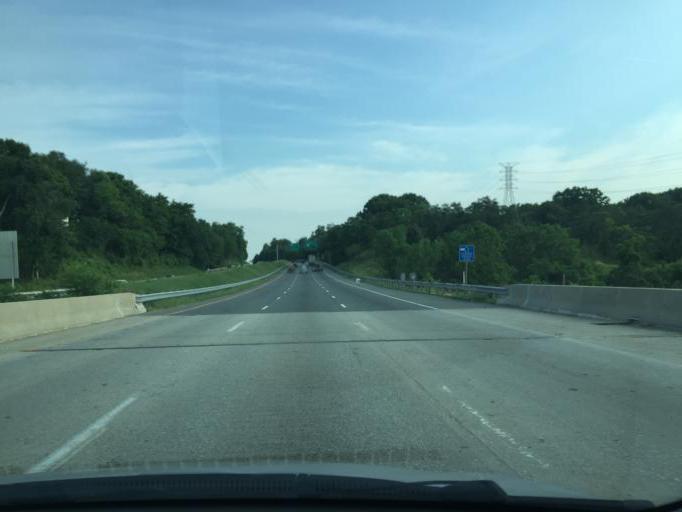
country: US
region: Maryland
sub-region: Baltimore County
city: Mays Chapel
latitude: 39.3847
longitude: -76.6622
